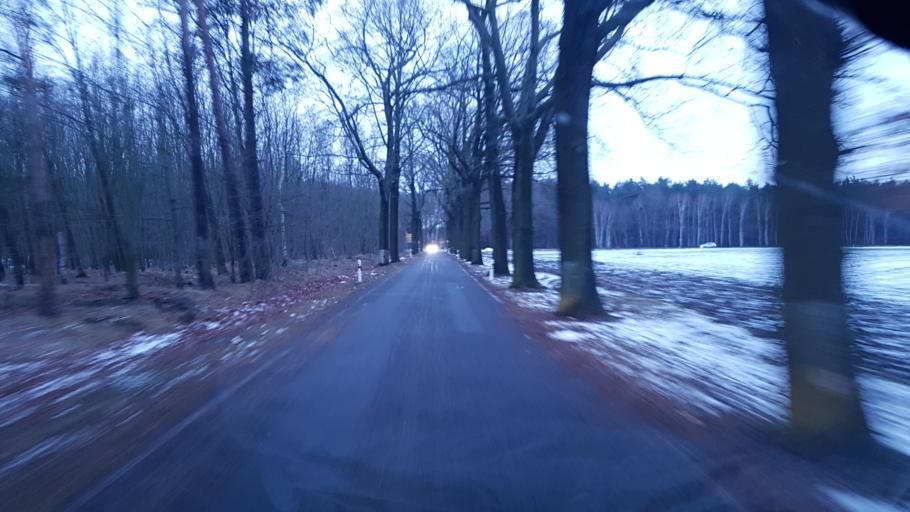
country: DE
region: Brandenburg
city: Neupetershain
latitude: 51.6120
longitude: 14.1373
